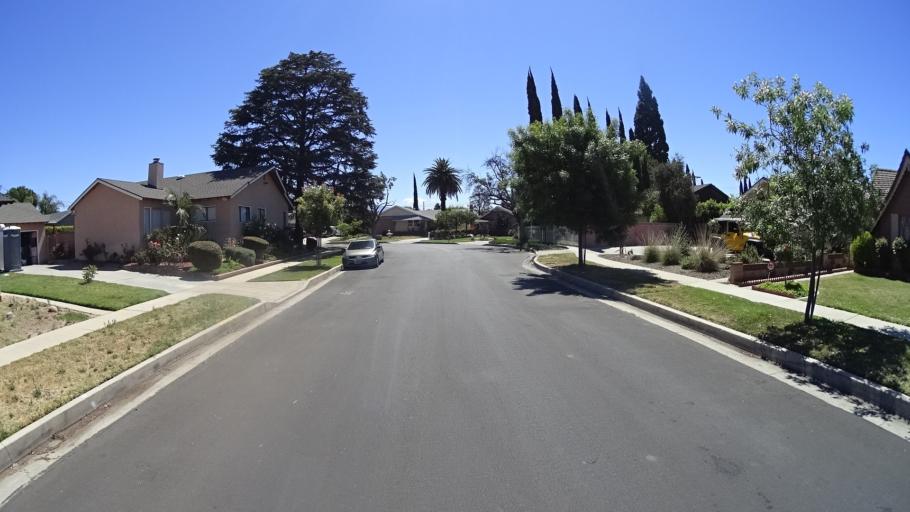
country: US
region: California
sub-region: Los Angeles County
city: San Fernando
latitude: 34.2508
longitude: -118.4648
